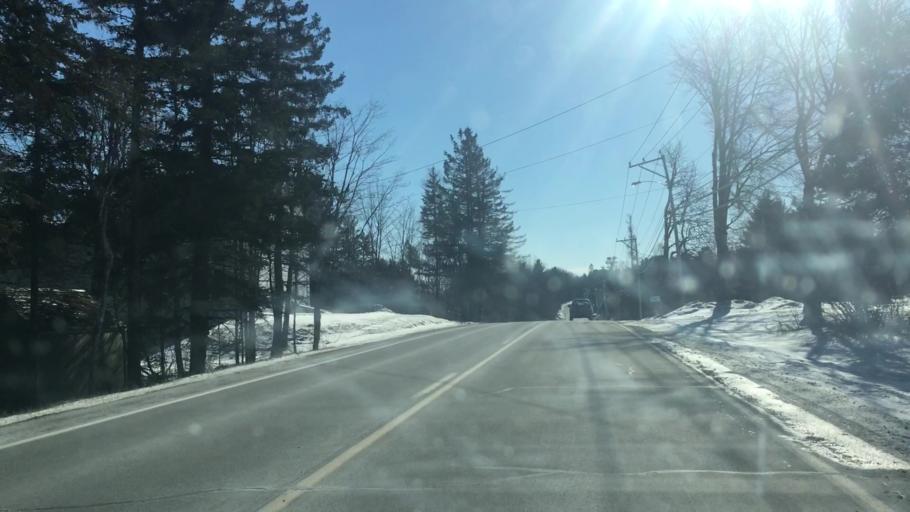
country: US
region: Maine
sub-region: Hancock County
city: Ellsworth
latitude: 44.5254
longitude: -68.4317
